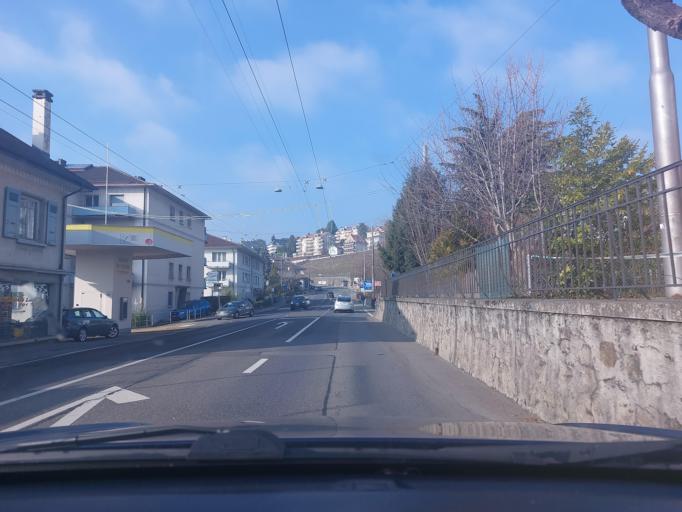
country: CH
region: Vaud
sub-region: Lavaux-Oron District
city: Paudex
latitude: 46.5076
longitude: 6.6712
